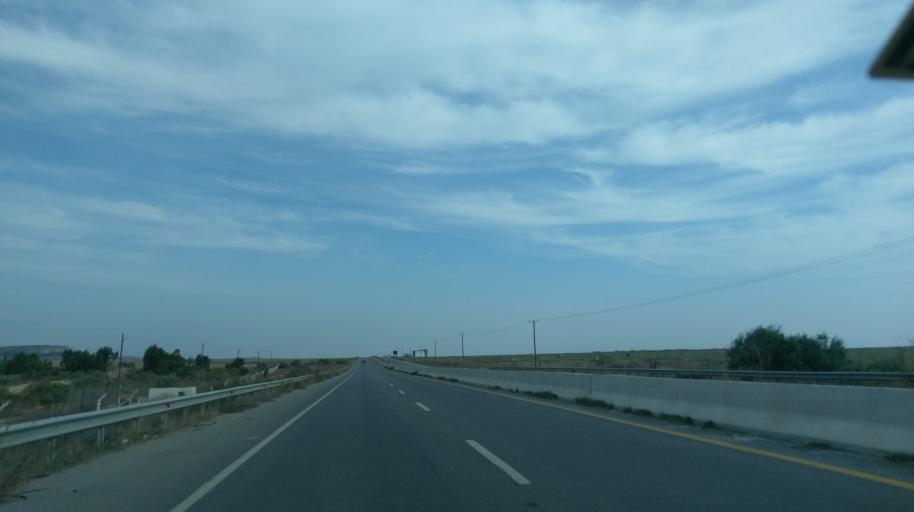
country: CY
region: Lefkosia
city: Mammari
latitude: 35.2142
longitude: 33.1886
